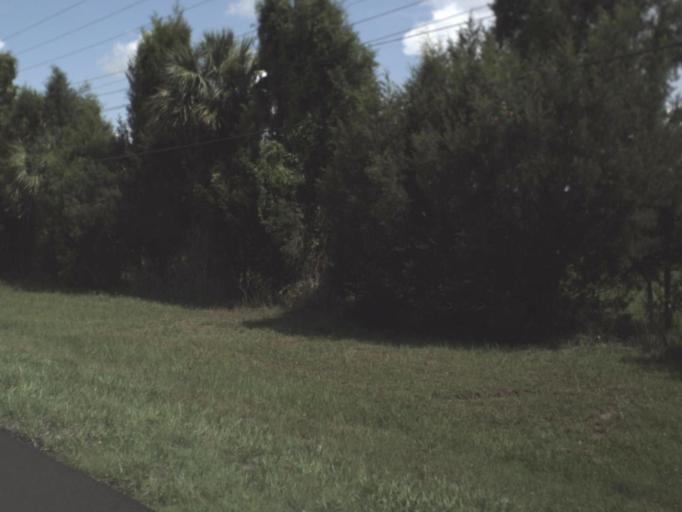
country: US
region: Florida
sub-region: Alachua County
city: Alachua
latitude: 29.7723
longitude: -82.4351
